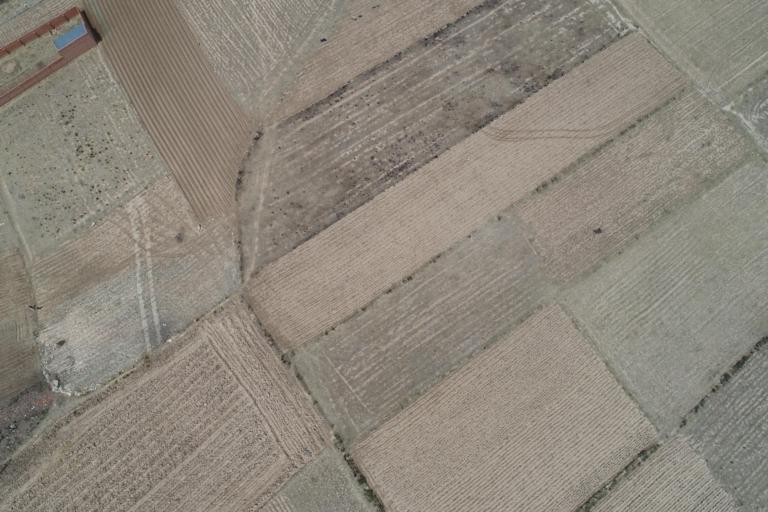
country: BO
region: La Paz
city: Achacachi
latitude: -16.0529
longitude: -68.6754
